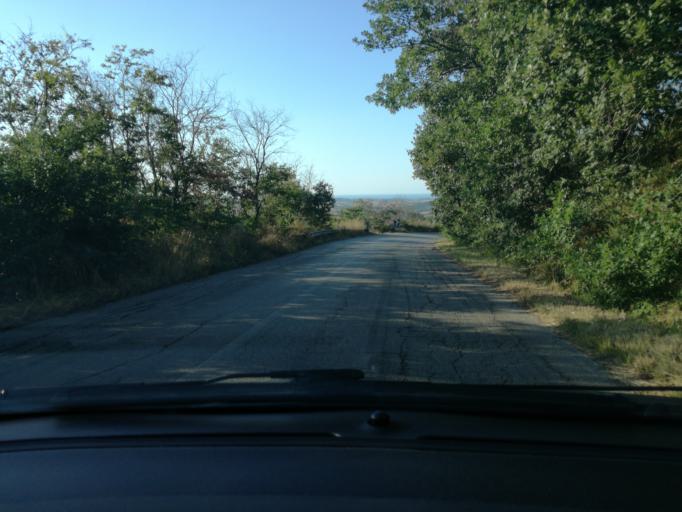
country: IT
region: Molise
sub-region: Provincia di Campobasso
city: Guglionesi
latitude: 41.9341
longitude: 14.9309
